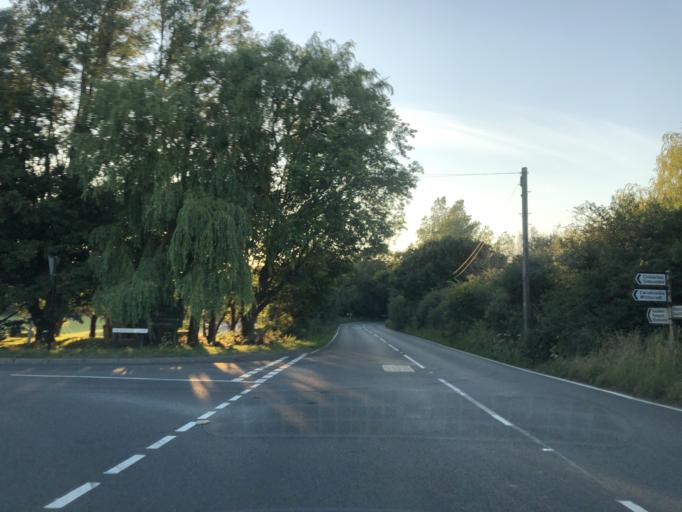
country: GB
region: England
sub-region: Isle of Wight
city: Newport
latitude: 50.6570
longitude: -1.2844
